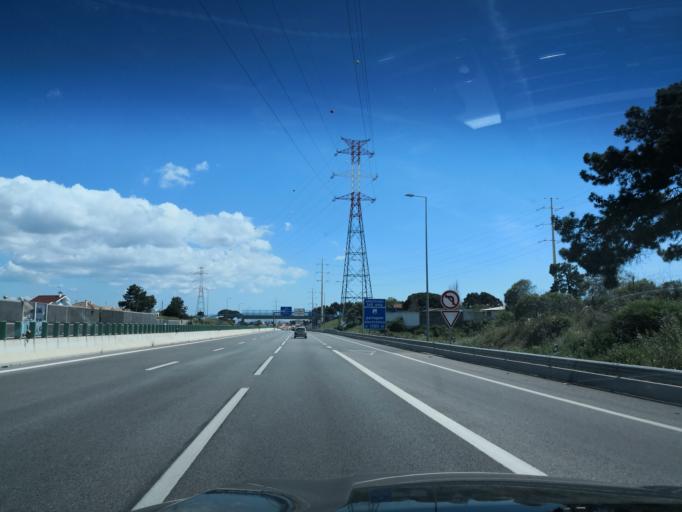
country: PT
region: Setubal
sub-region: Almada
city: Charneca
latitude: 38.6293
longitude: -9.1940
